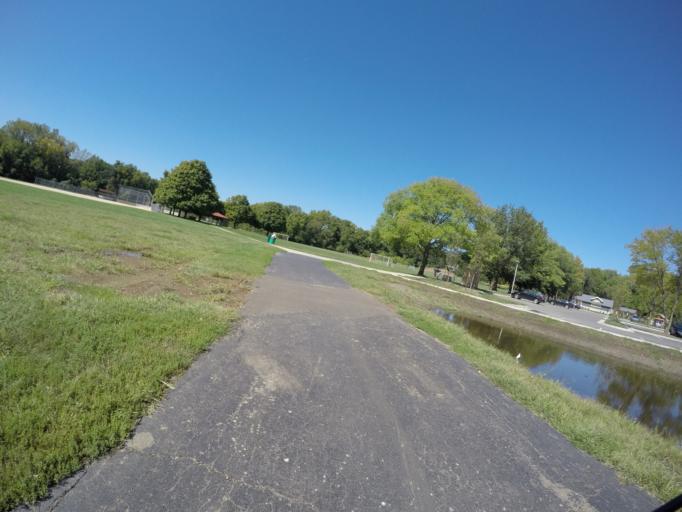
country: US
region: Kansas
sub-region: Johnson County
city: Leawood
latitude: 38.9395
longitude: -94.6411
